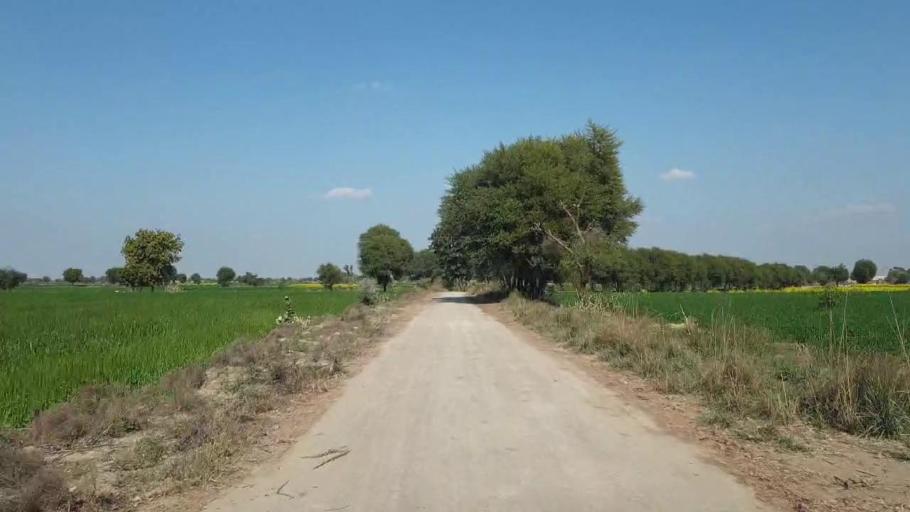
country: PK
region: Sindh
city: Shahpur Chakar
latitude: 26.0798
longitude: 68.5850
